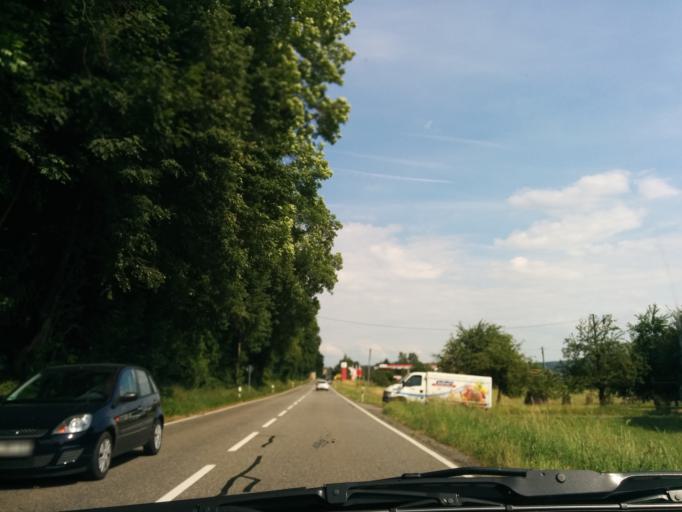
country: DE
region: Saxony
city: Floha
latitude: 50.8656
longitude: 13.0549
